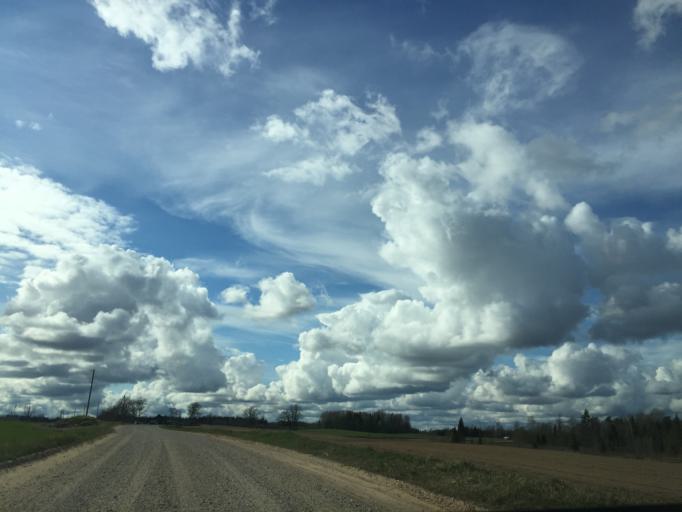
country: LV
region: Burtnieki
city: Matisi
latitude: 57.6106
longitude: 25.0325
